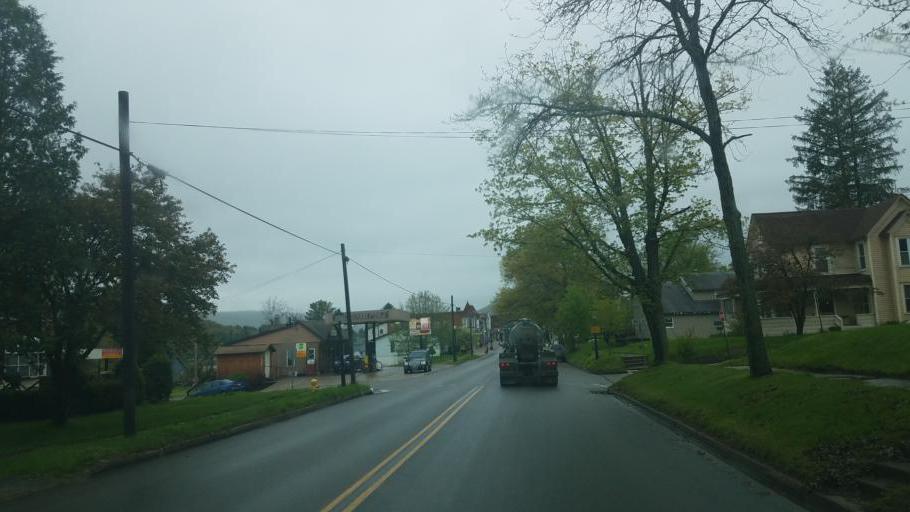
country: US
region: Pennsylvania
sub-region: McKean County
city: Smethport
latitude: 41.8104
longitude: -78.4401
